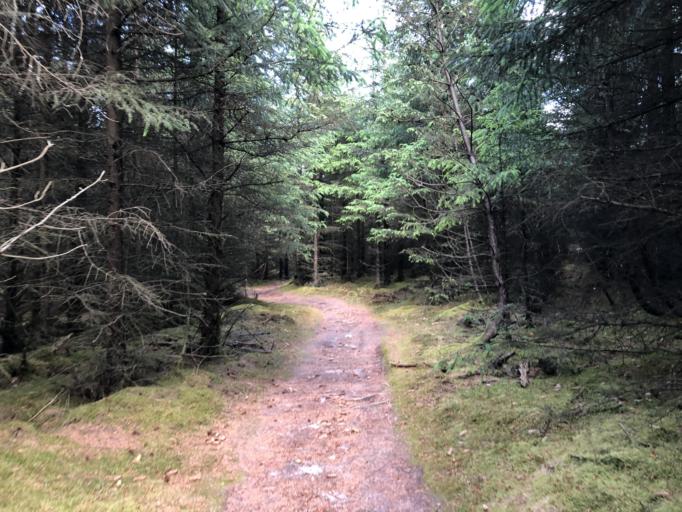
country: DK
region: Central Jutland
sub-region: Lemvig Kommune
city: Lemvig
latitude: 56.4901
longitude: 8.3753
